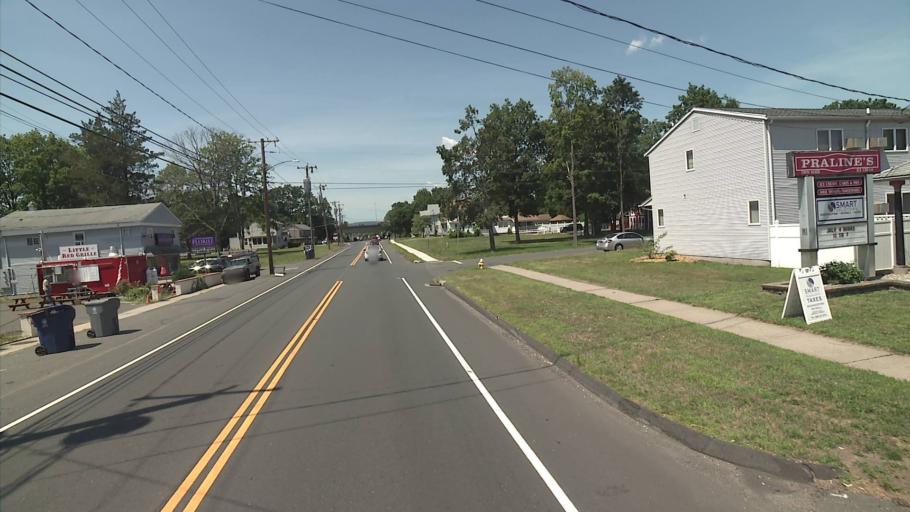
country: US
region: Connecticut
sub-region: Hartford County
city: Plainville
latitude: 41.6766
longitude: -72.8513
